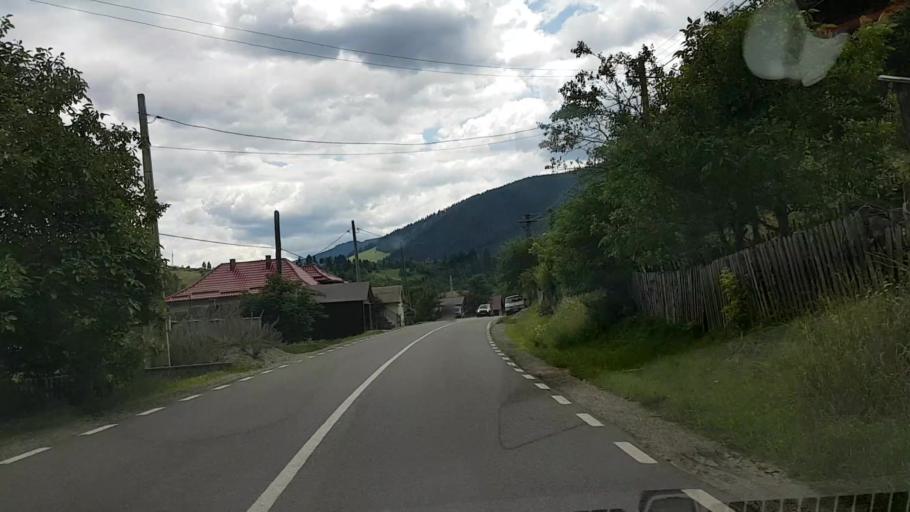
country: RO
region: Neamt
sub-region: Comuna Borca
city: Borca
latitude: 47.2139
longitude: 25.7558
